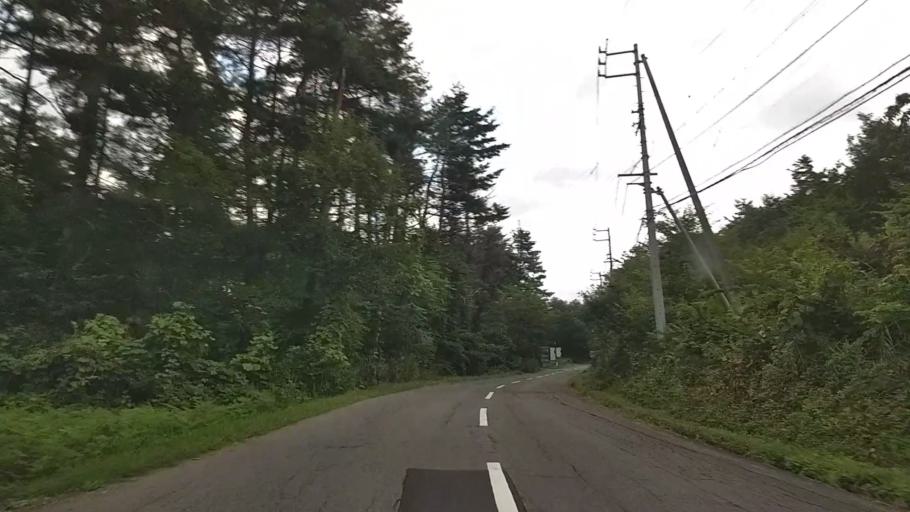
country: JP
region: Nagano
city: Iiyama
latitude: 36.8209
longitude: 138.3982
